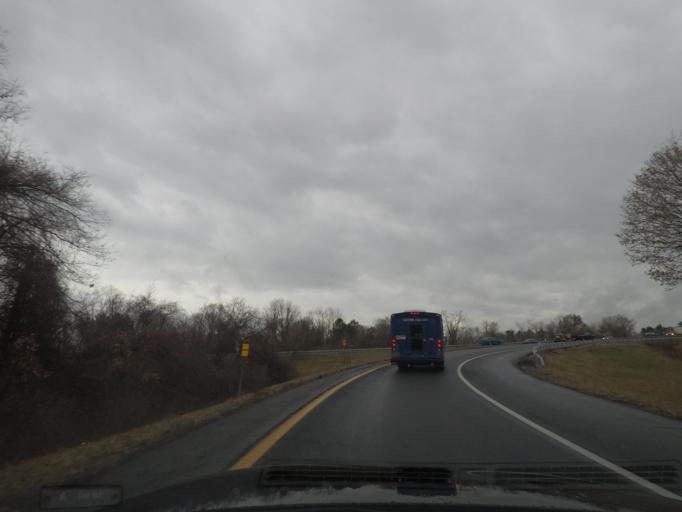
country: US
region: New York
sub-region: Albany County
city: Colonie
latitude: 42.7127
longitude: -73.8227
